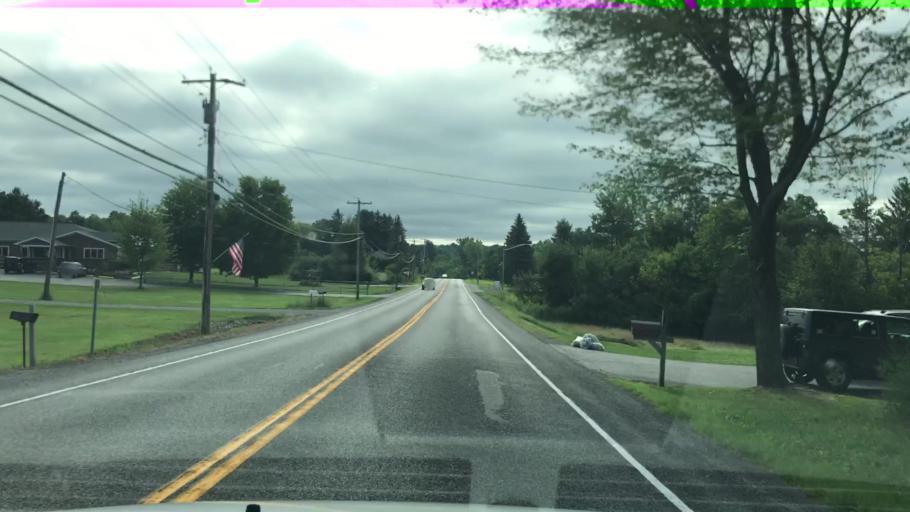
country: US
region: New York
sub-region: Erie County
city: Alden
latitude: 42.8367
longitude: -78.3941
